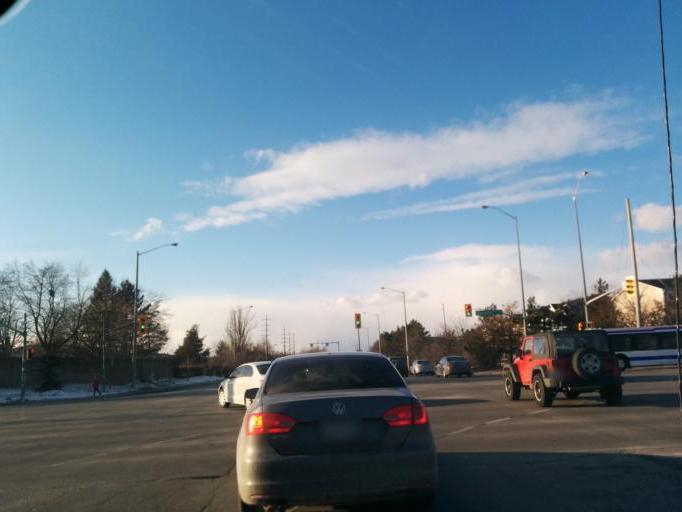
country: CA
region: Ontario
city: Brampton
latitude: 43.6563
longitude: -79.7434
